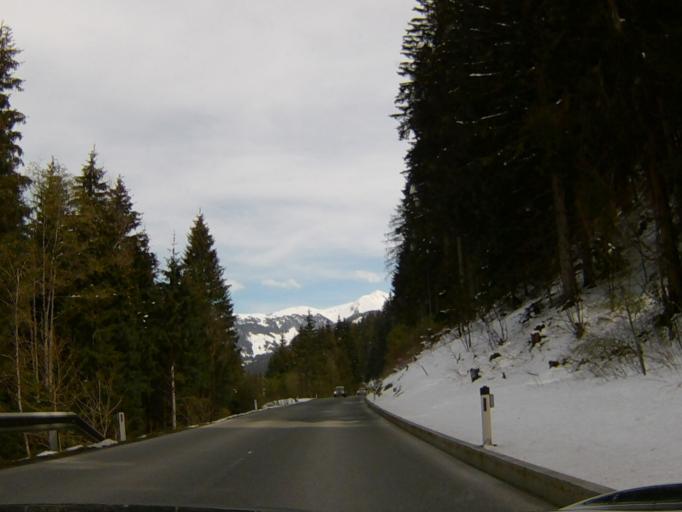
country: AT
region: Tyrol
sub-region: Politischer Bezirk Schwaz
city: Gerlosberg
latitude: 47.2110
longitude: 11.9483
